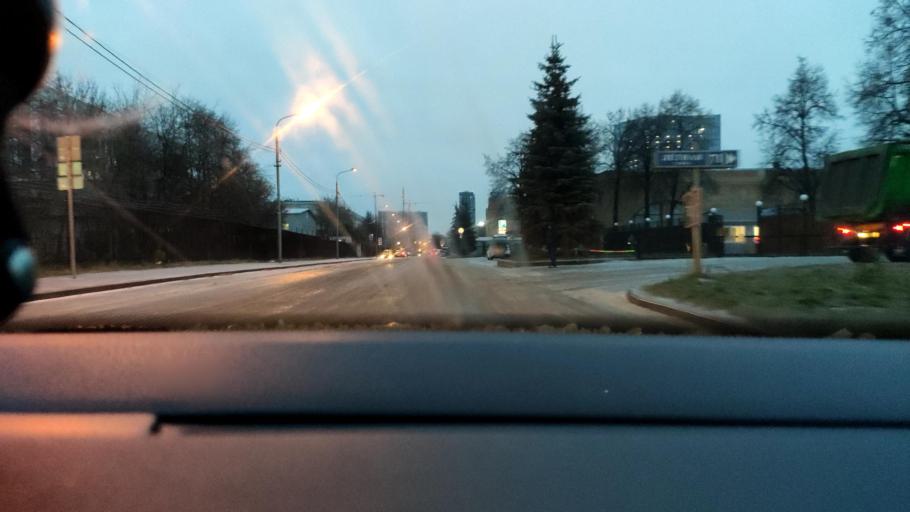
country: RU
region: Moscow
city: Strogino
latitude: 55.8256
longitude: 37.4199
